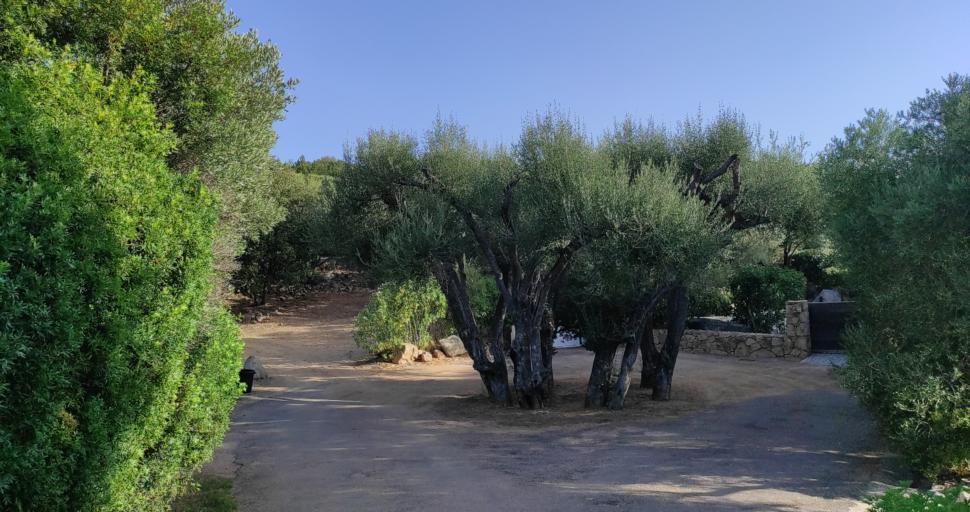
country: FR
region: Corsica
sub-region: Departement de la Corse-du-Sud
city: Porto-Vecchio
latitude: 41.6220
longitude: 9.3509
